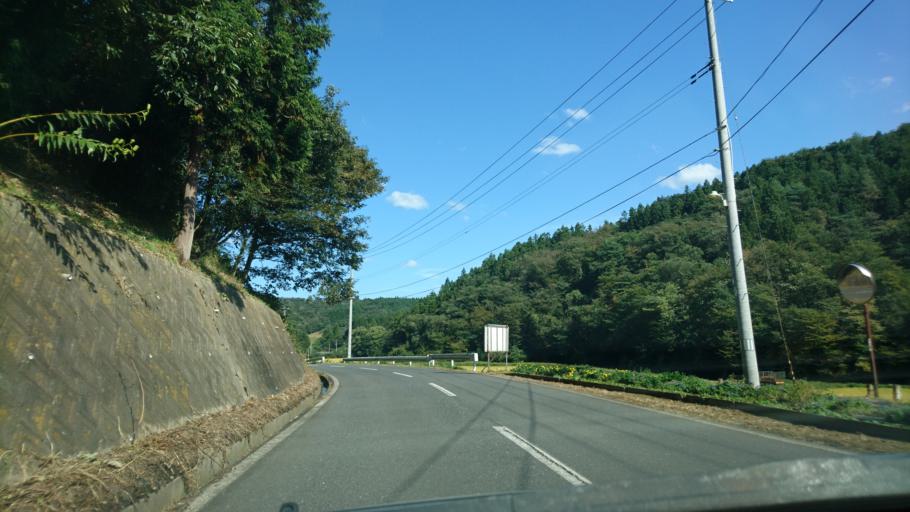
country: JP
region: Iwate
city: Ichinoseki
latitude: 38.8965
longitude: 141.0369
